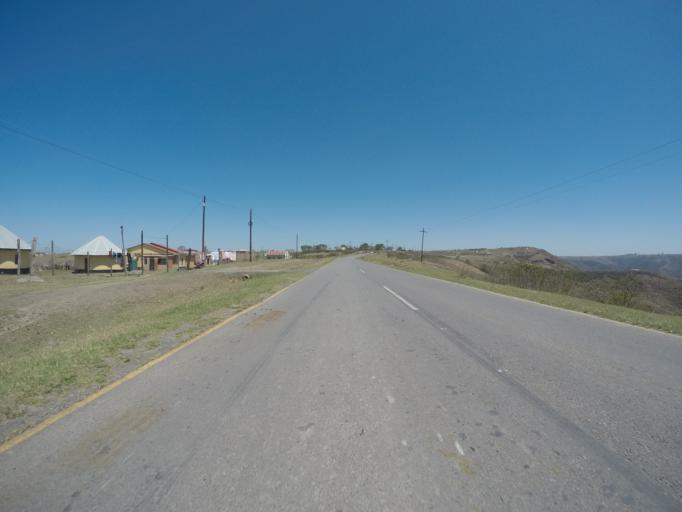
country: ZA
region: Eastern Cape
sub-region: OR Tambo District Municipality
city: Libode
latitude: -31.9114
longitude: 28.9950
